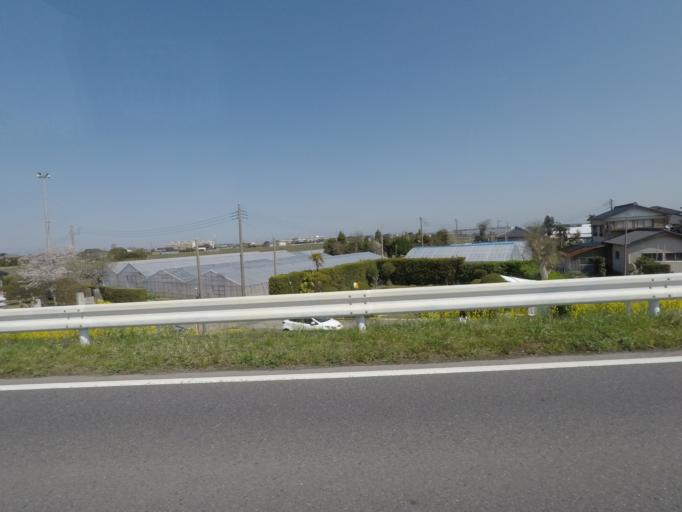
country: JP
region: Chiba
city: Katori-shi
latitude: 35.9204
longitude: 140.4619
